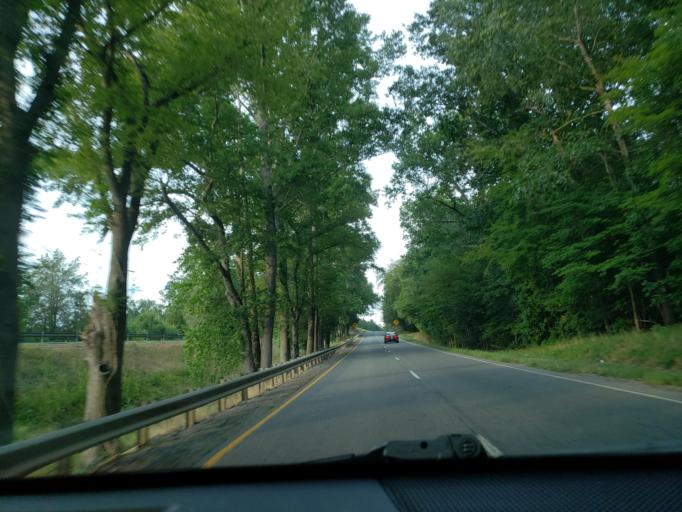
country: US
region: Virginia
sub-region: Brunswick County
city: Lawrenceville
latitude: 36.7412
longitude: -77.8919
